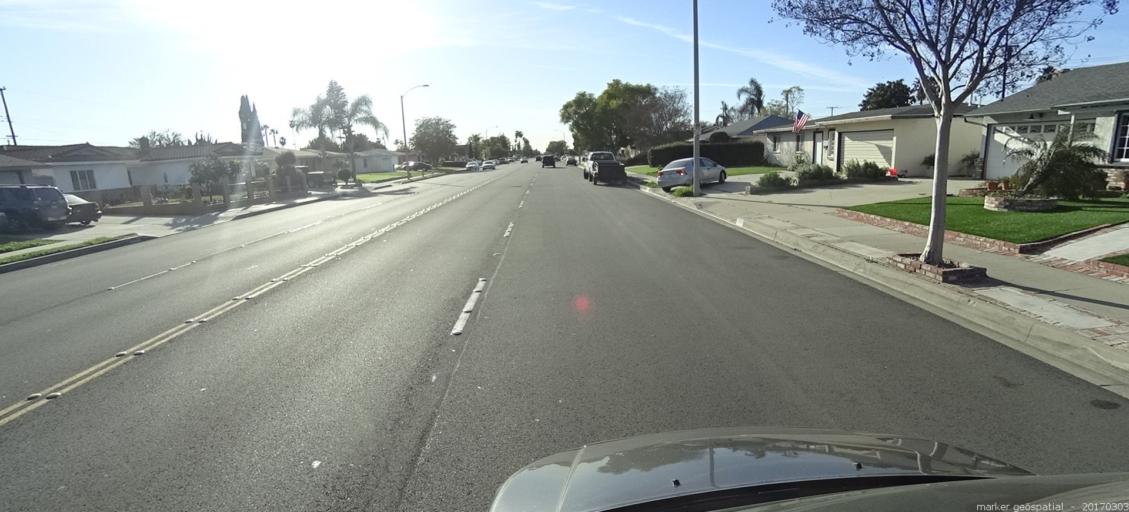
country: US
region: California
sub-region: Orange County
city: Anaheim
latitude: 33.8289
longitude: -117.9465
